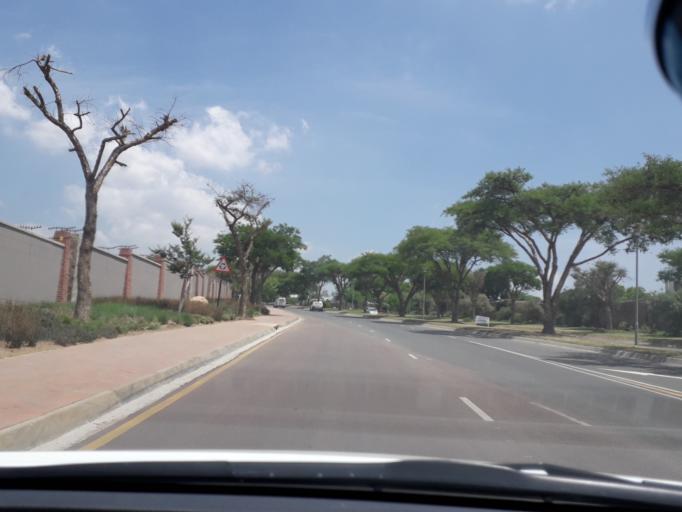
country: ZA
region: Gauteng
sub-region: City of Johannesburg Metropolitan Municipality
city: Midrand
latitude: -26.0234
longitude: 28.0849
